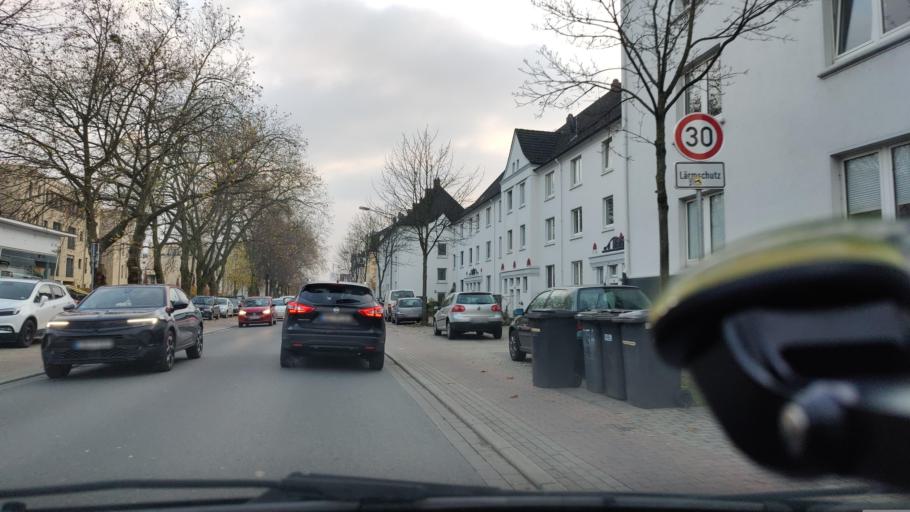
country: DE
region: North Rhine-Westphalia
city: Lunen
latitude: 51.6235
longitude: 7.5255
